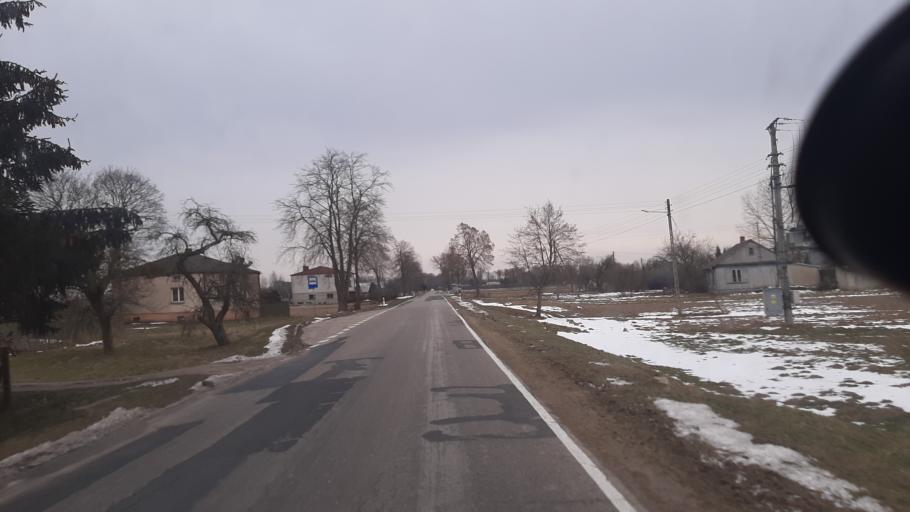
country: PL
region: Lublin Voivodeship
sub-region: Powiat lubartowski
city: Kamionka
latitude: 51.4548
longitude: 22.4211
